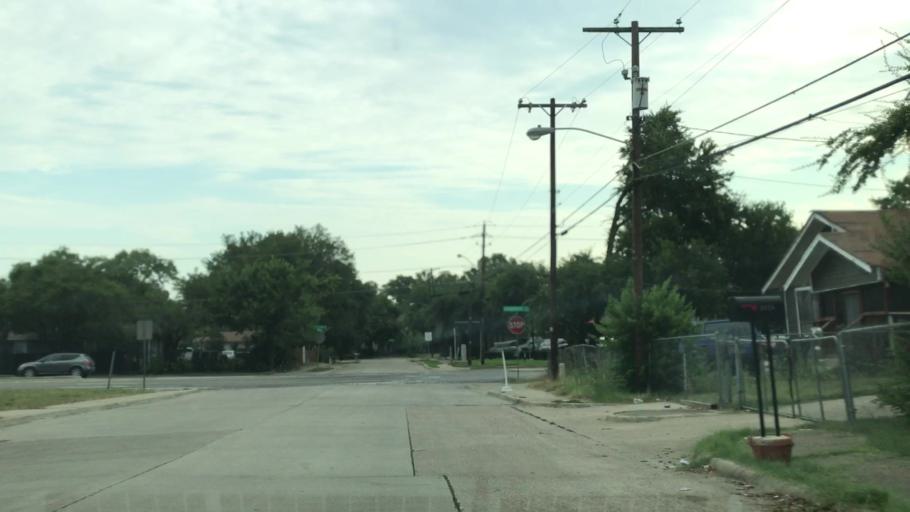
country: US
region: Texas
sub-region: Dallas County
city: Cockrell Hill
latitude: 32.7781
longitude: -96.9120
